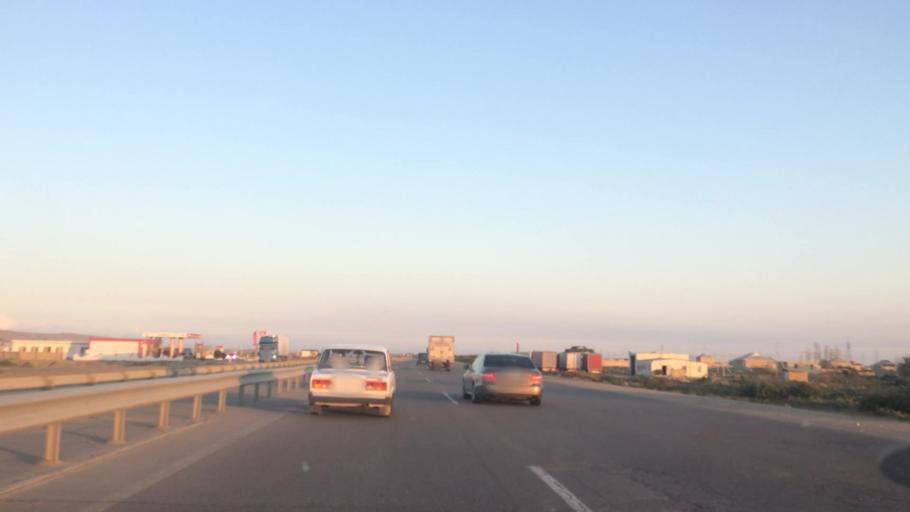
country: AZ
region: Baki
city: Qobustan
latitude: 39.9692
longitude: 49.2676
